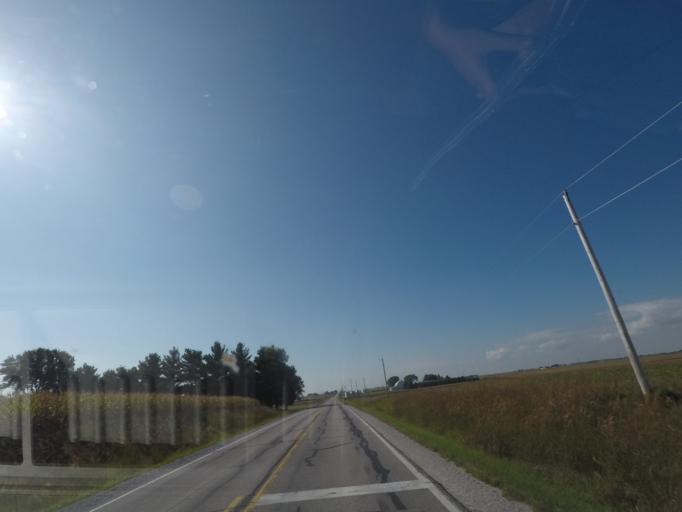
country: US
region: Iowa
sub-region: Story County
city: Nevada
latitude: 42.0265
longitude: -93.4058
